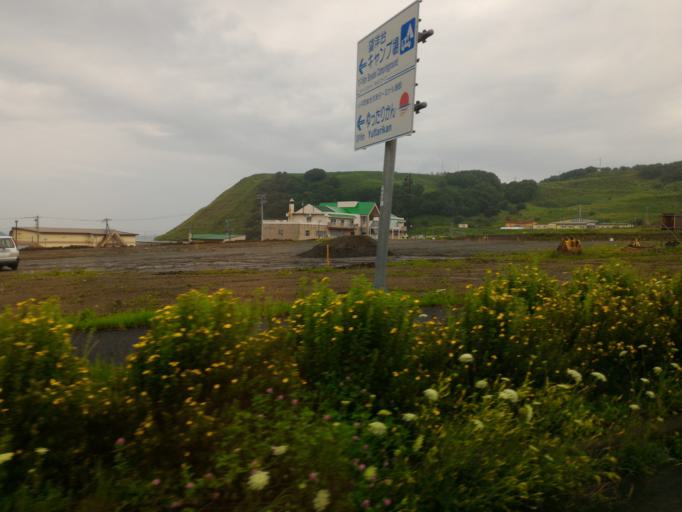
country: JP
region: Hokkaido
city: Rumoi
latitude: 44.0265
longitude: 141.6671
